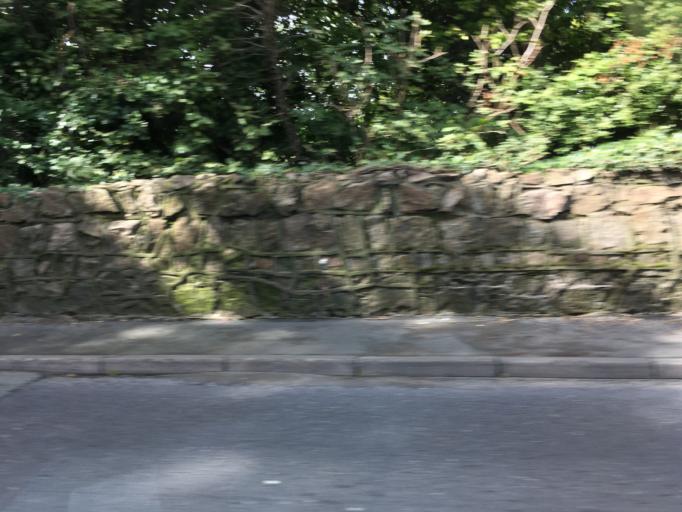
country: IE
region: Leinster
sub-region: Wicklow
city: Kilmacanoge
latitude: 53.1832
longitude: -6.1310
